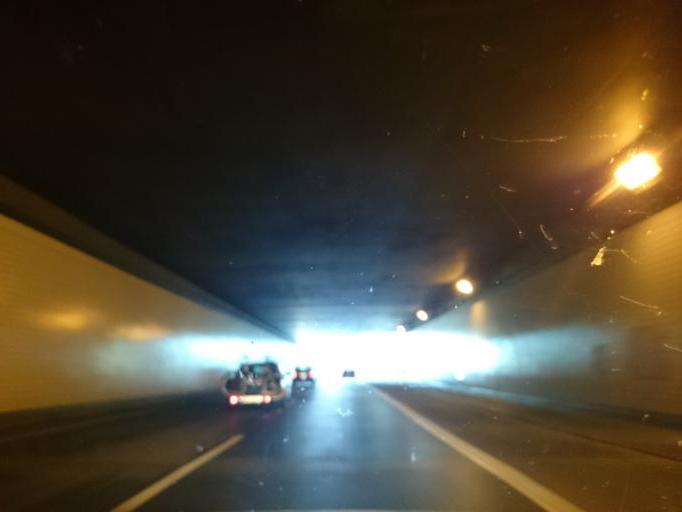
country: DE
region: Berlin
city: Tegel
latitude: 52.5826
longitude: 13.2938
